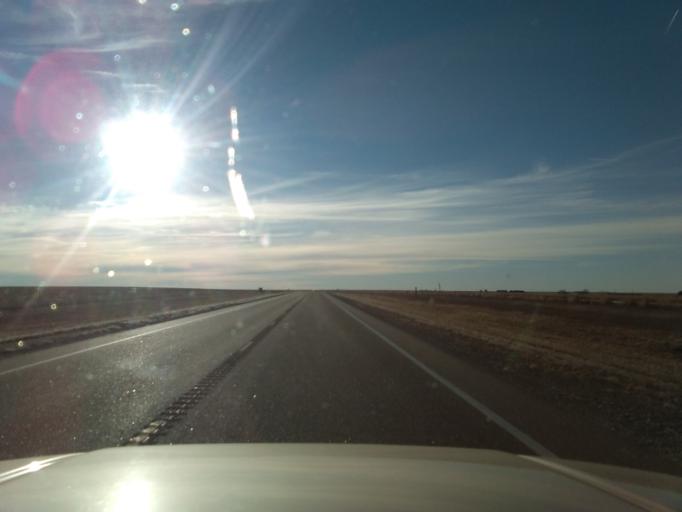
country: US
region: Kansas
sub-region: Sheridan County
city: Hoxie
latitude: 39.5158
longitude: -100.6333
